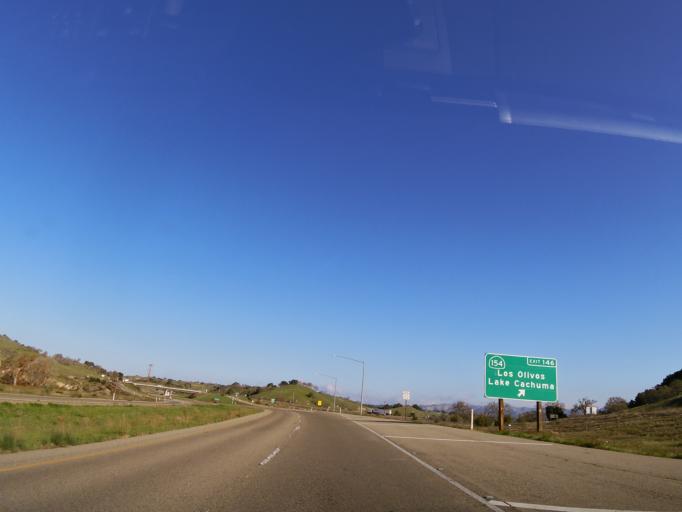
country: US
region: California
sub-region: Santa Barbara County
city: Los Olivos
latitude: 34.6834
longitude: -120.1566
